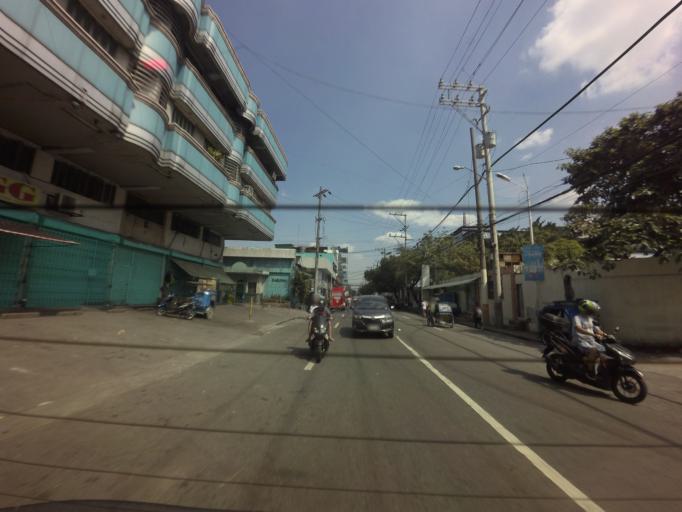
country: PH
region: Metro Manila
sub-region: City of Manila
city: Manila
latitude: 14.6109
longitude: 120.9725
